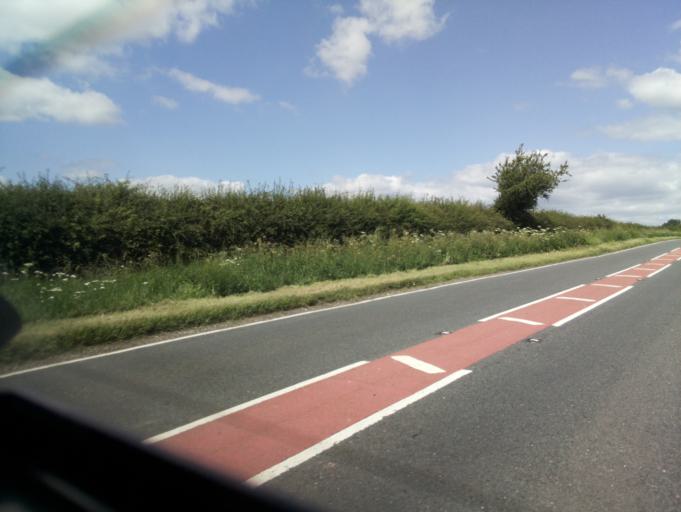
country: GB
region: England
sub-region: Buckinghamshire
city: Aylesbury
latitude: 51.8472
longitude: -0.8244
